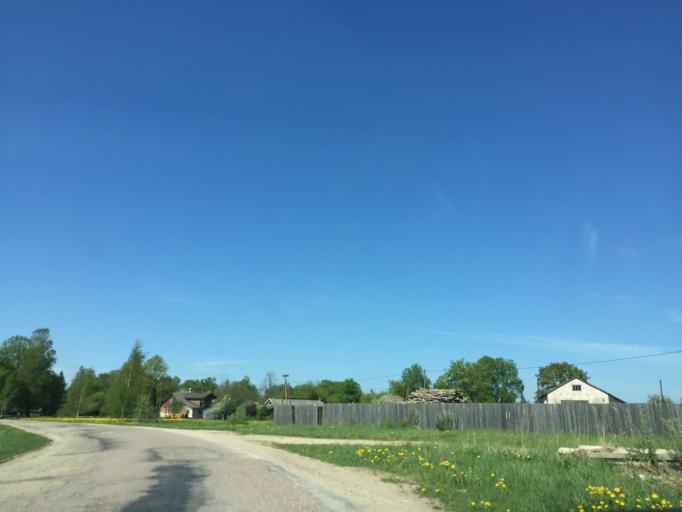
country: LV
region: Ogre
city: Ogre
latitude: 56.8568
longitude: 24.7020
